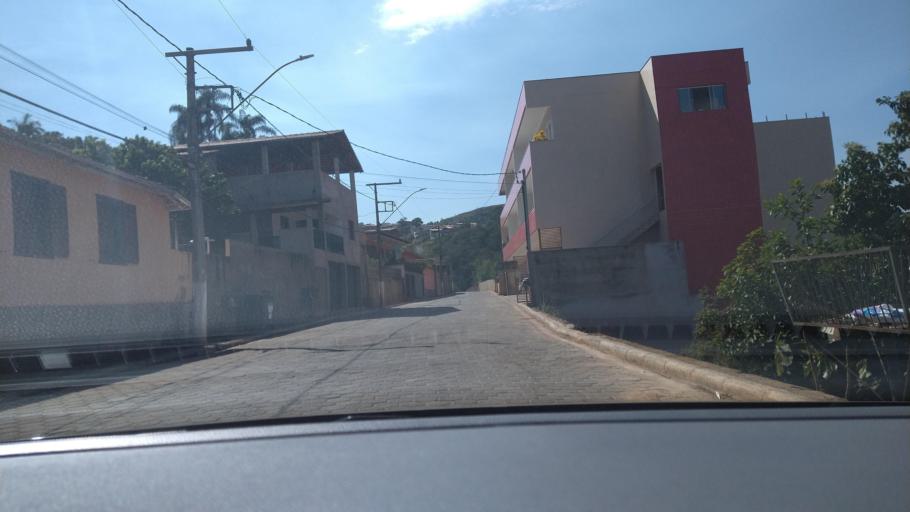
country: BR
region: Minas Gerais
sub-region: Rio Piracicaba
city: Rio Piracicaba
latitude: -19.9301
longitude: -43.1748
